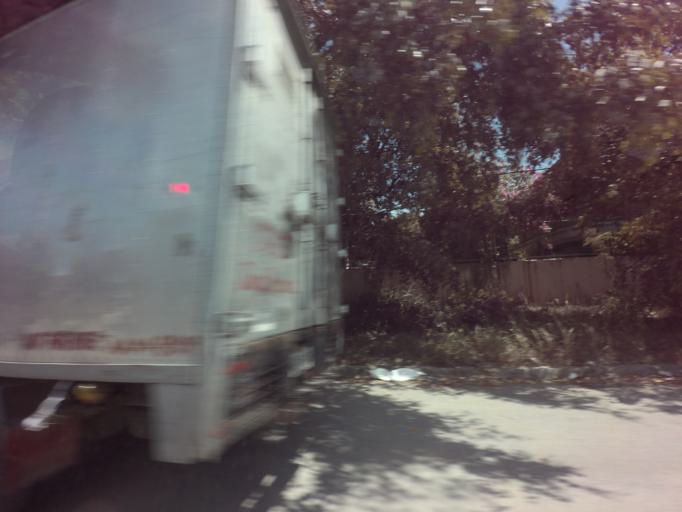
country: PH
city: Sambayanihan People's Village
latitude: 14.5073
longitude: 120.9844
